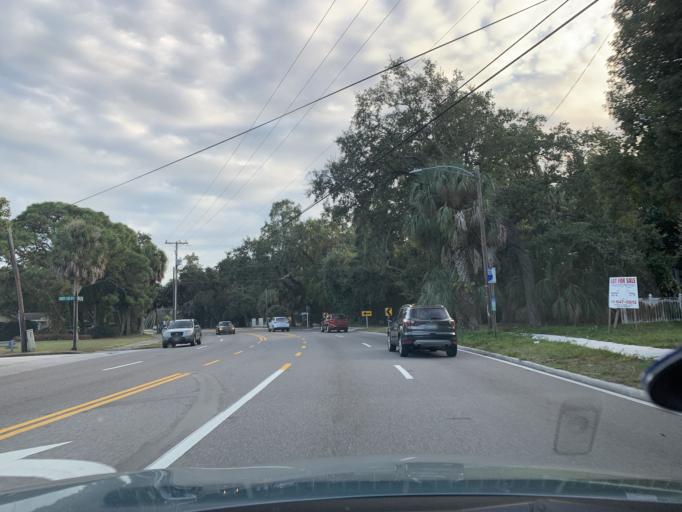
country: US
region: Florida
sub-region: Pinellas County
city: Treasure Island
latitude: 27.7916
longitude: -82.7539
